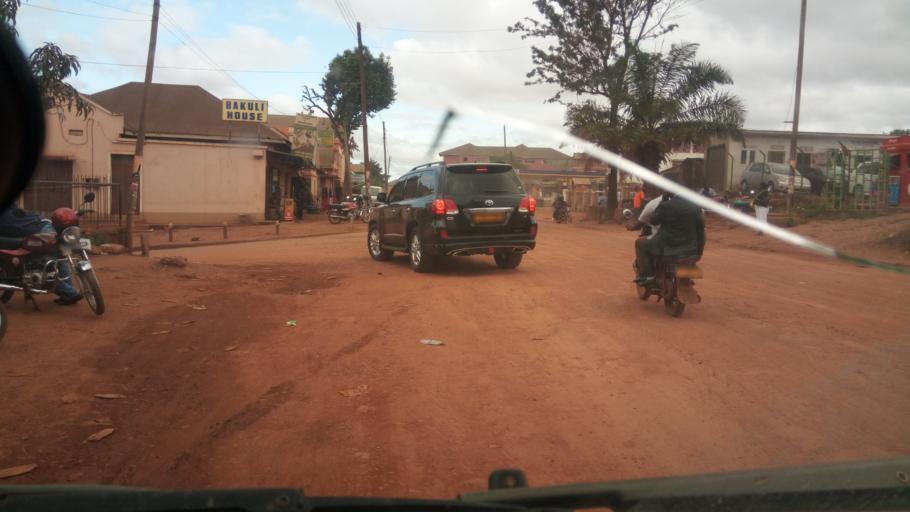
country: UG
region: Central Region
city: Kampala Central Division
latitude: 0.3171
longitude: 32.5640
